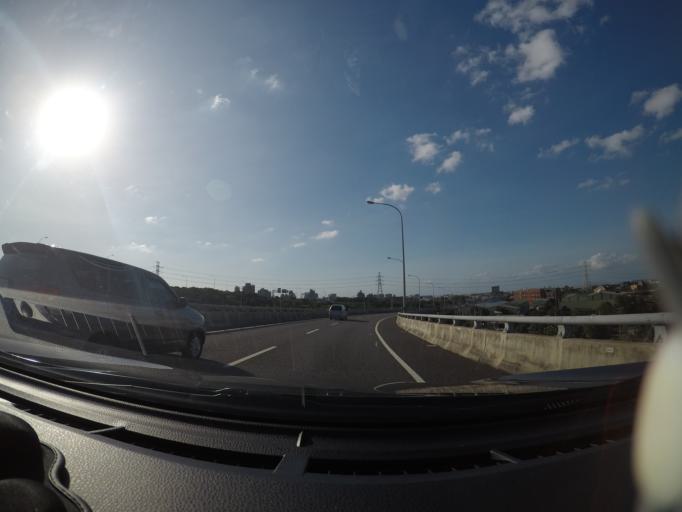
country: TW
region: Taiwan
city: Taoyuan City
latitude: 25.0211
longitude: 121.2726
